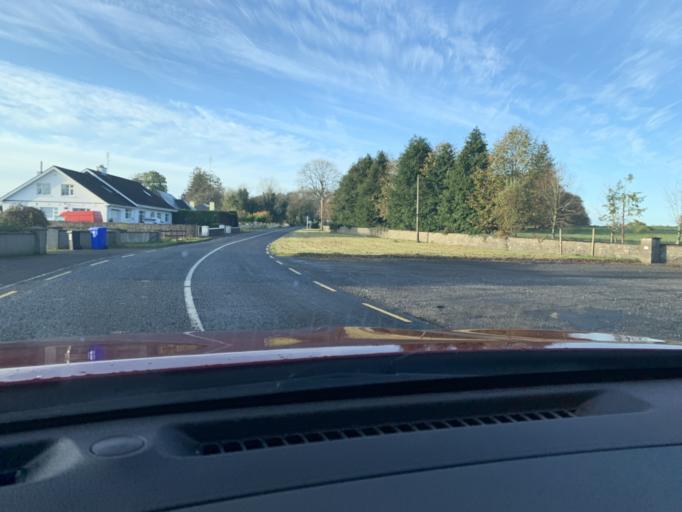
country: IE
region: Connaught
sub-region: Roscommon
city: Ballaghaderreen
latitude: 53.9197
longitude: -8.5367
